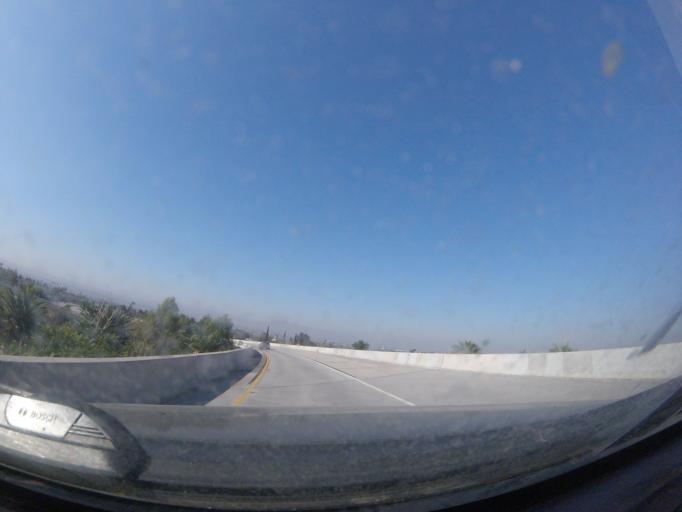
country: US
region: California
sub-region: San Bernardino County
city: Highland
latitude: 34.1299
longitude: -117.2034
